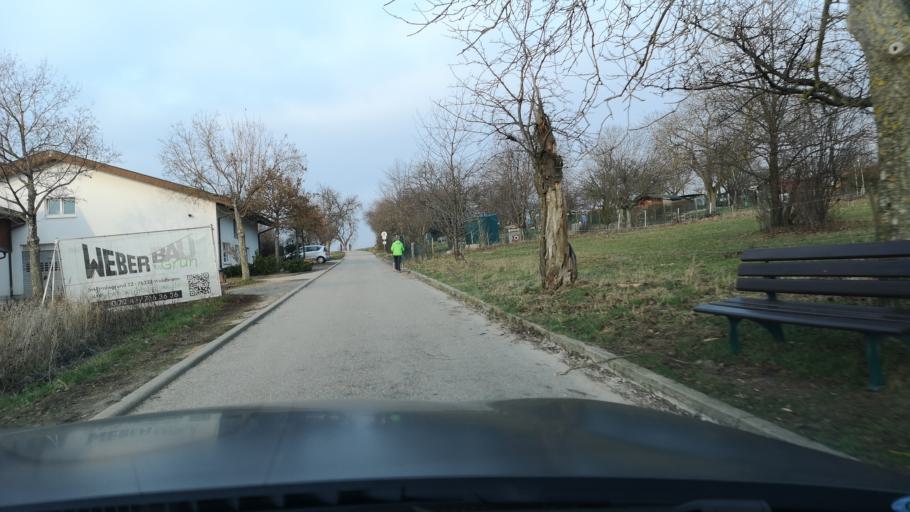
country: DE
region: Baden-Wuerttemberg
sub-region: Karlsruhe Region
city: Ettlingen
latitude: 48.9349
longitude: 8.4676
